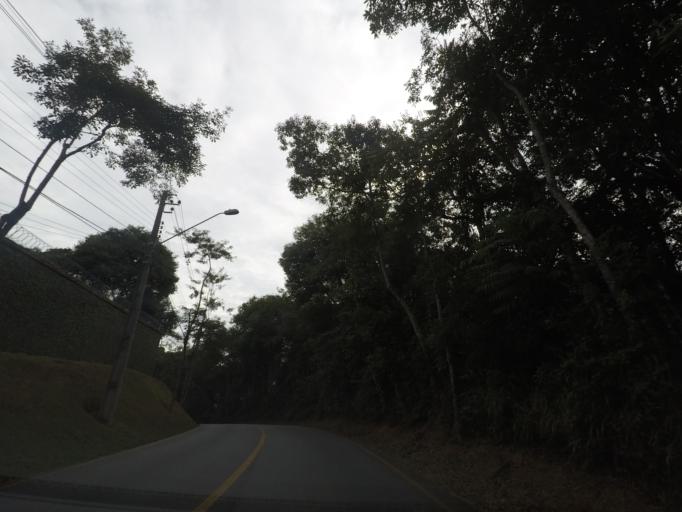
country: BR
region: Parana
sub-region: Curitiba
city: Curitiba
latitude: -25.3988
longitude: -49.3048
